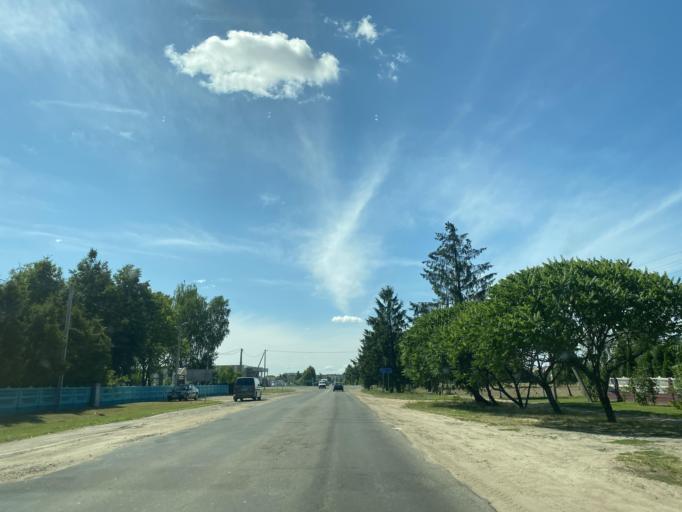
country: BY
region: Brest
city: Ivanava
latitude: 52.1593
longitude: 25.5457
